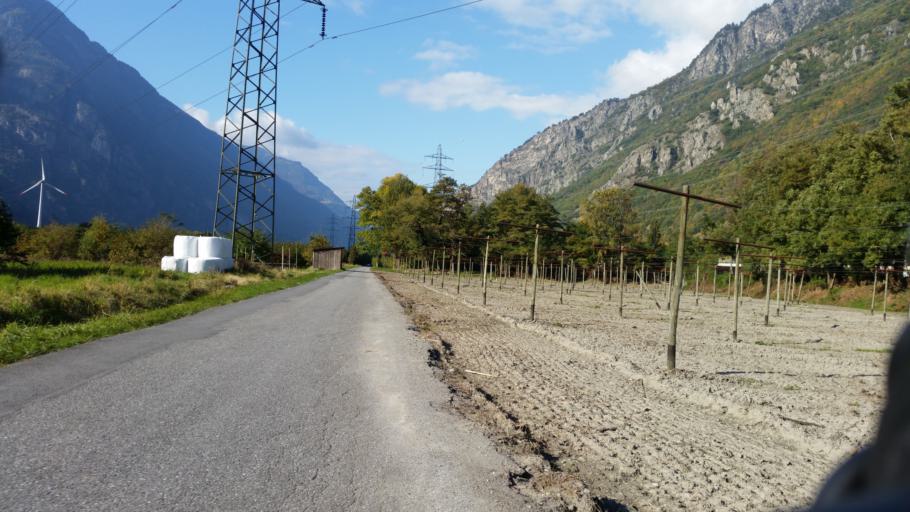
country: CH
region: Valais
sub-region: Martigny District
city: Martigny-Ville
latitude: 46.1195
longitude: 7.0667
